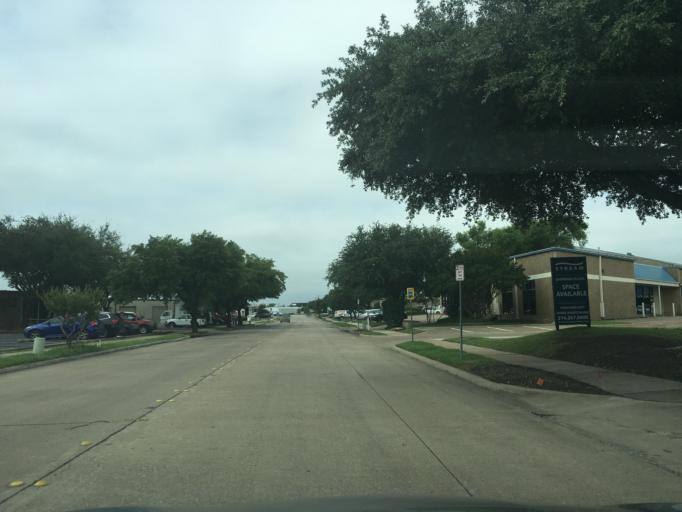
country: US
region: Texas
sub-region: Dallas County
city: Richardson
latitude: 32.9446
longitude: -96.7370
